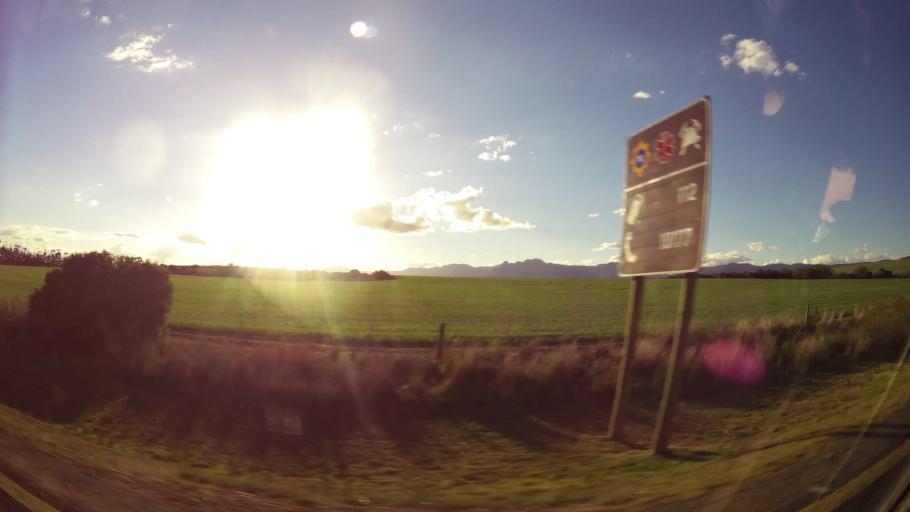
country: ZA
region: Western Cape
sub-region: Eden District Municipality
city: Riversdale
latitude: -34.0874
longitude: 20.9811
